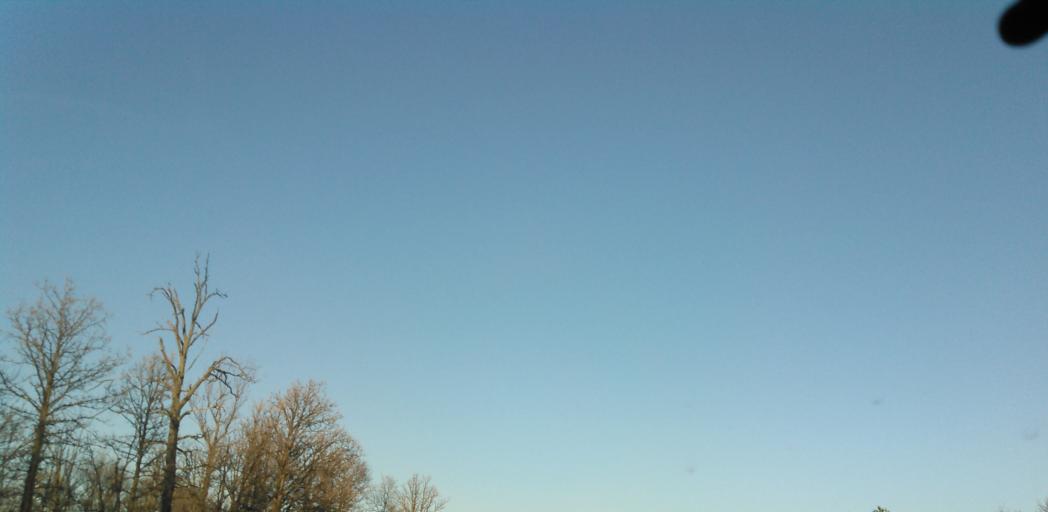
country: US
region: New York
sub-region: Monroe County
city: Pittsford
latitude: 43.0471
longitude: -77.5764
